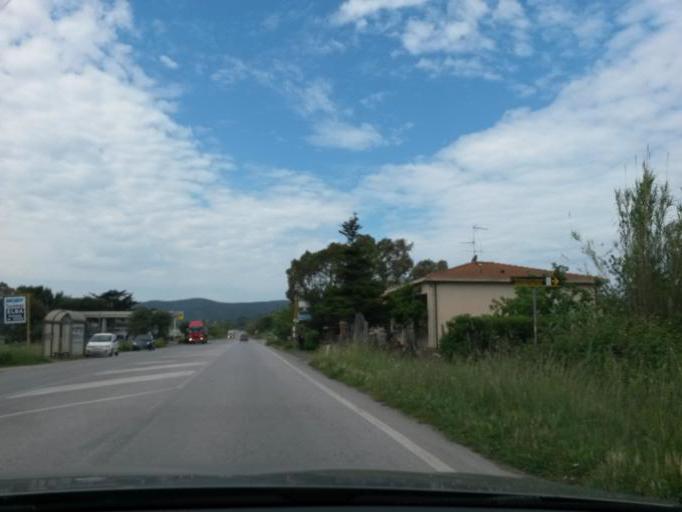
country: IT
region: Tuscany
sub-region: Provincia di Livorno
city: Piombino
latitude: 42.9676
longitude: 10.5505
